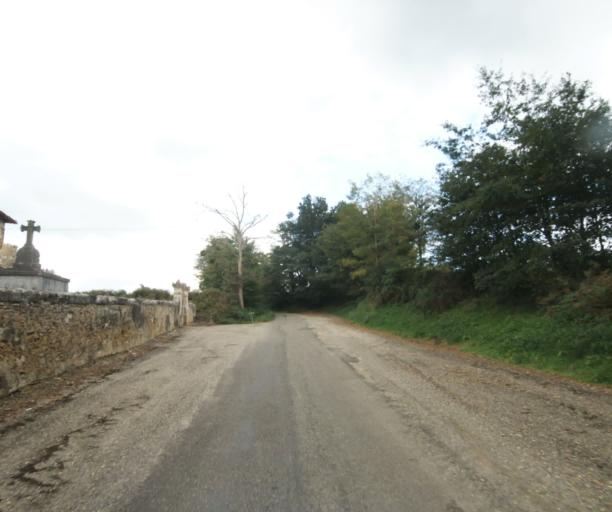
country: FR
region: Midi-Pyrenees
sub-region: Departement du Gers
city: Eauze
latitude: 43.9379
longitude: 0.0783
